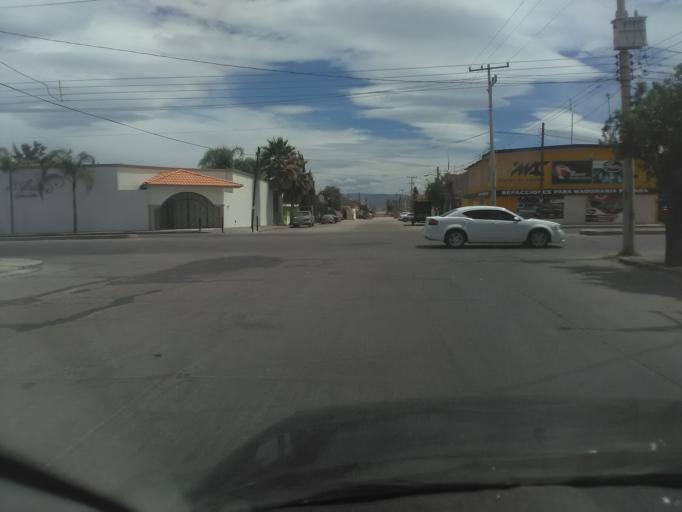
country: MX
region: Durango
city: Victoria de Durango
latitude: 24.0201
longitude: -104.6311
